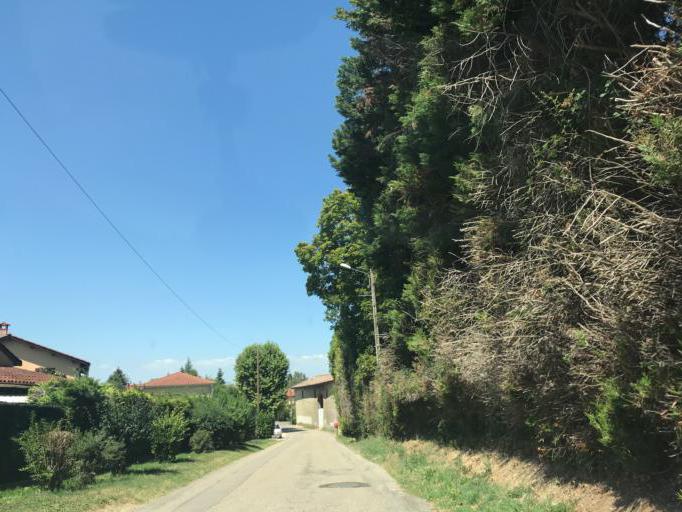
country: FR
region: Rhone-Alpes
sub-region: Departement de l'Ain
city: Tramoyes
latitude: 45.8786
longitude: 4.9662
